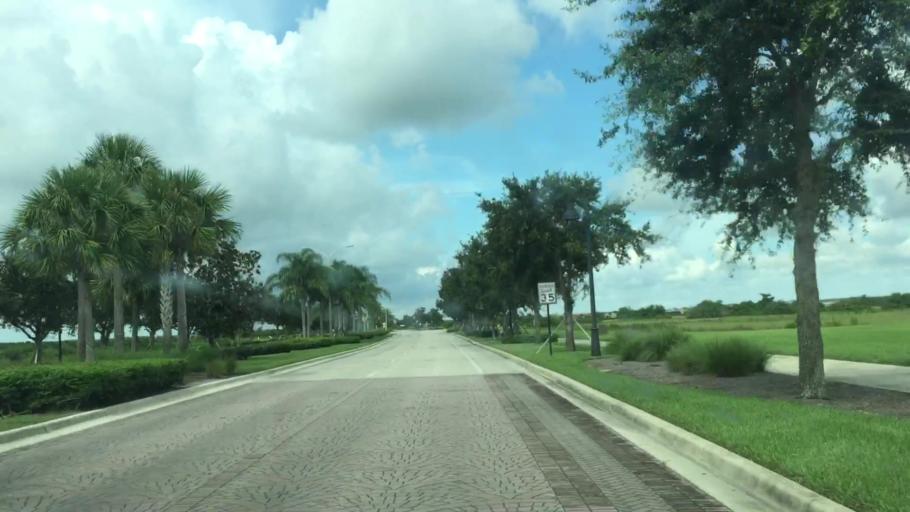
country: US
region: Florida
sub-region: Collier County
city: Immokalee
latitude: 26.3392
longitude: -81.4174
